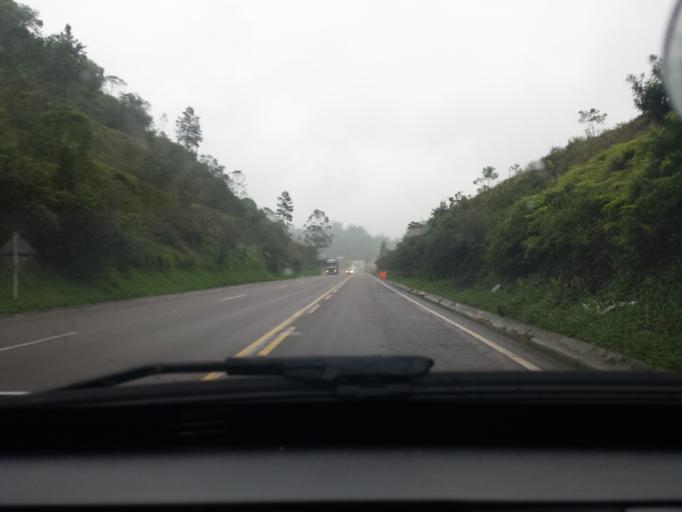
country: BR
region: Santa Catarina
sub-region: Itajai
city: Itajai
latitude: -26.8377
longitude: -48.7751
